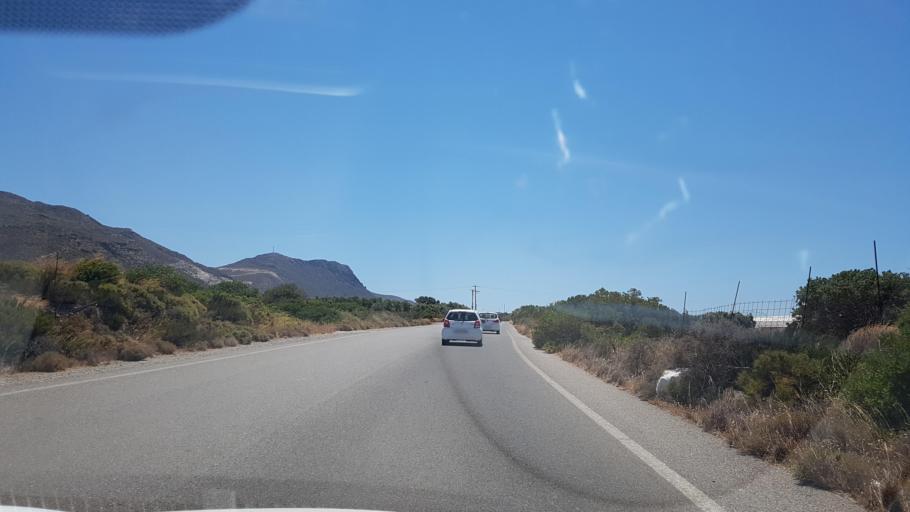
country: GR
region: Crete
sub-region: Nomos Chanias
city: Palaiochora
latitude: 35.2921
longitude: 23.5452
